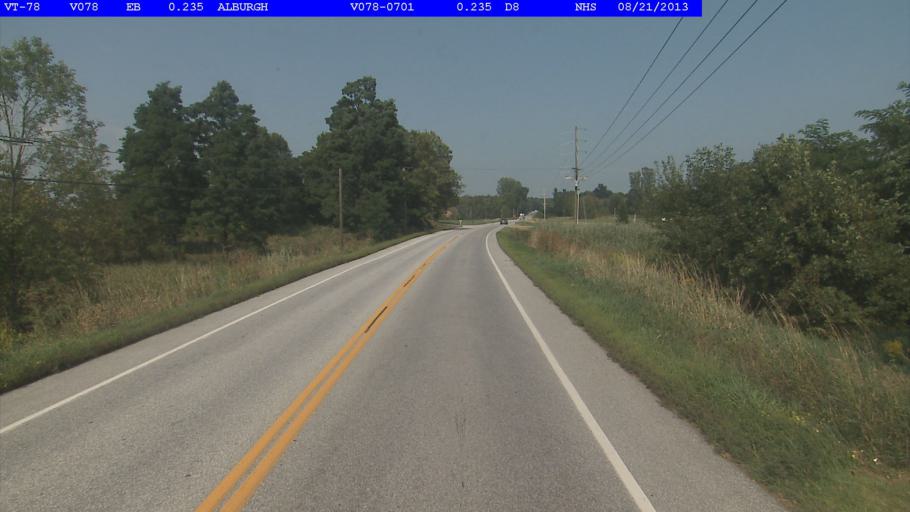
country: US
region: New York
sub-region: Clinton County
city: Rouses Point
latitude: 44.9627
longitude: -73.2746
